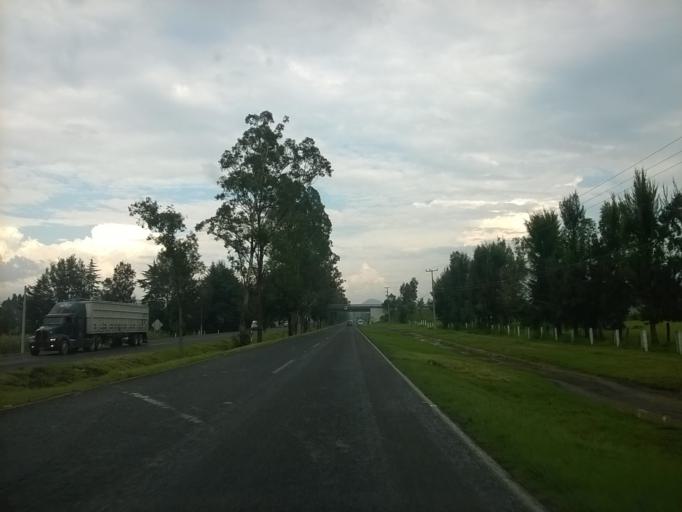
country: MX
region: Michoacan
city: Cuanajo
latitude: 19.5375
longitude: -101.5252
